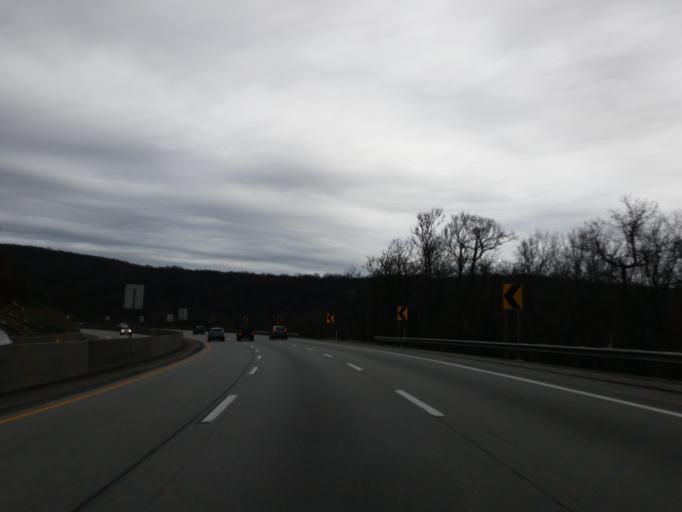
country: US
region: Pennsylvania
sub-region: Westmoreland County
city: Ligonier
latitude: 40.1212
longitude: -79.2793
